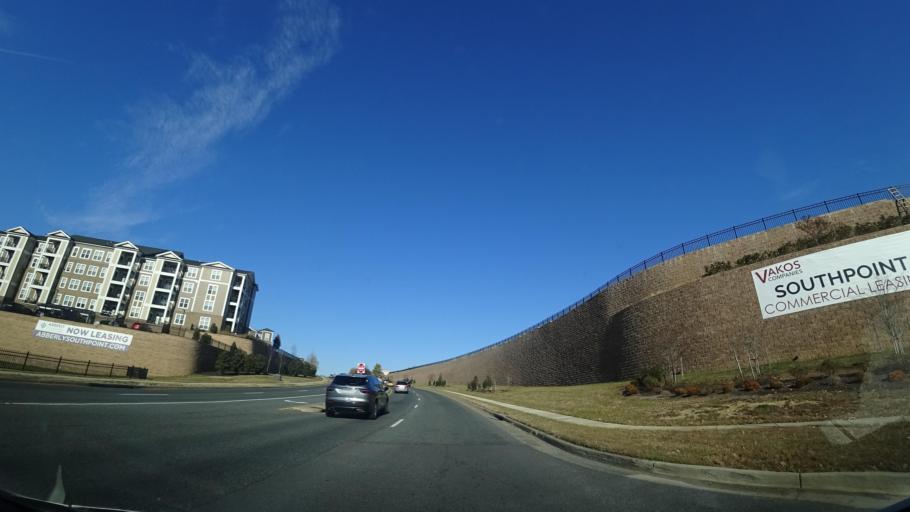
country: US
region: Virginia
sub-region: City of Fredericksburg
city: Fredericksburg
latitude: 38.2422
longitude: -77.5053
